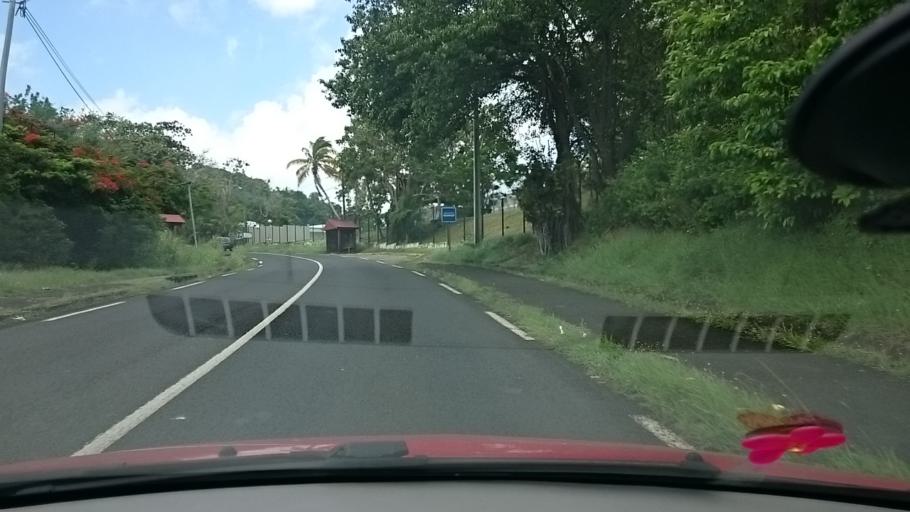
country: MQ
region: Martinique
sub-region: Martinique
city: La Trinite
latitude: 14.7417
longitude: -60.9481
